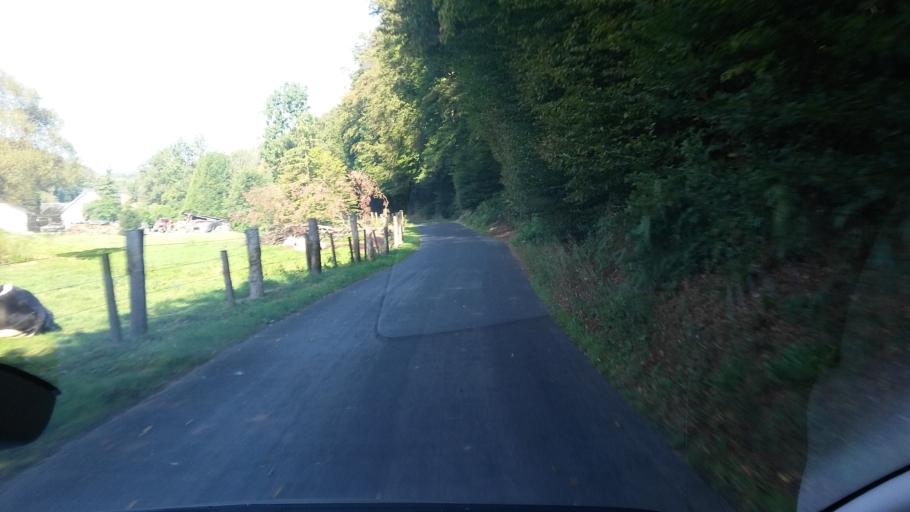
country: LU
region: Luxembourg
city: Eischen
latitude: 49.6995
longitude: 5.8576
